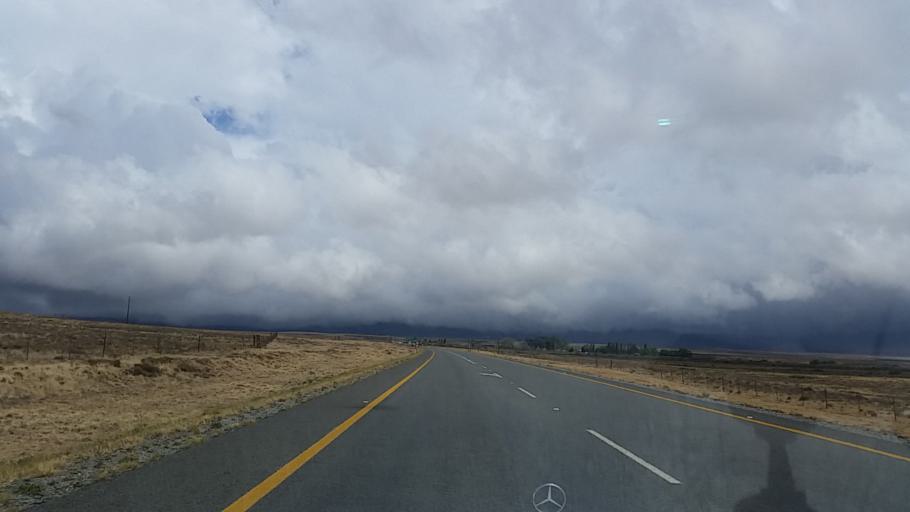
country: ZA
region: Eastern Cape
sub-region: Cacadu District Municipality
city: Graaff-Reinet
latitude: -31.8919
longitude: 24.7936
